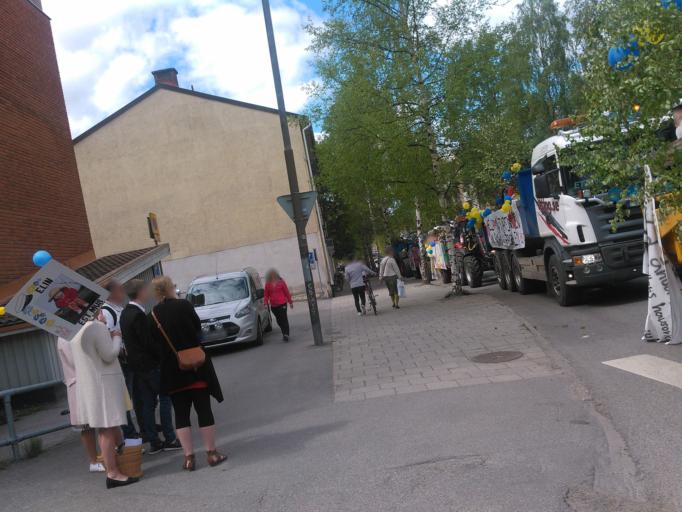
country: SE
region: Vaesterbotten
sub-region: Umea Kommun
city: Umea
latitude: 63.8271
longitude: 20.2721
